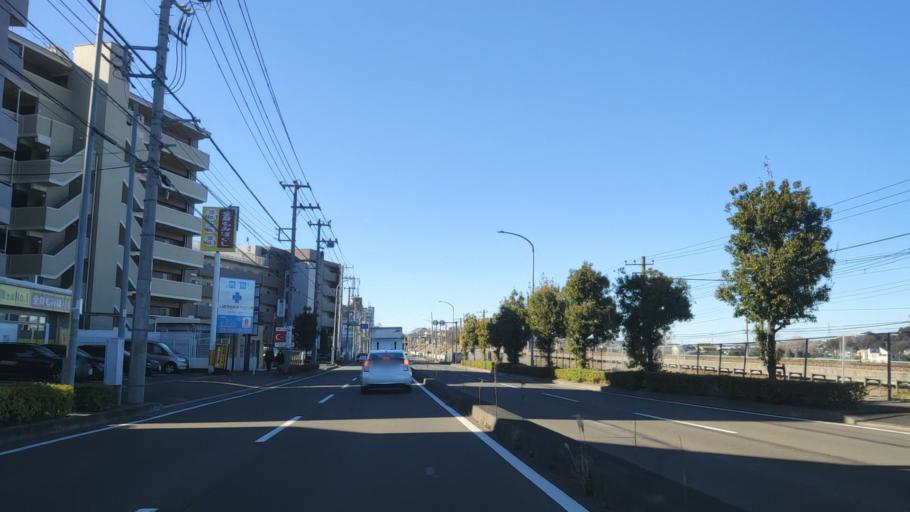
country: JP
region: Tokyo
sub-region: Machida-shi
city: Machida
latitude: 35.5179
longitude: 139.5327
